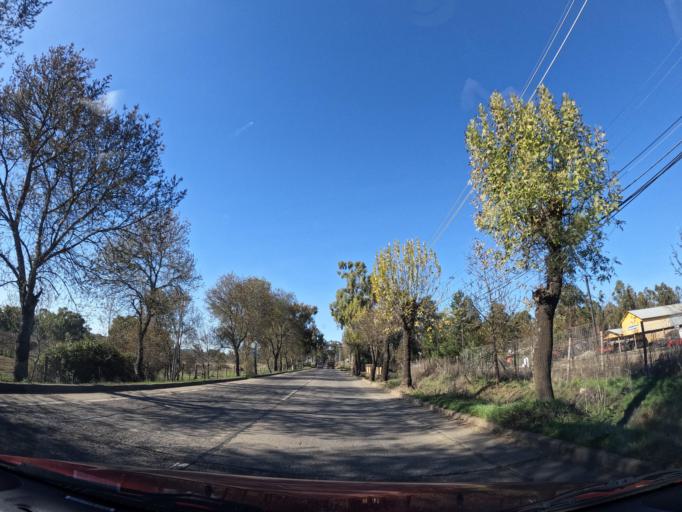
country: CL
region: Maule
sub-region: Provincia de Cauquenes
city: Cauquenes
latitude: -35.9579
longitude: -72.2950
